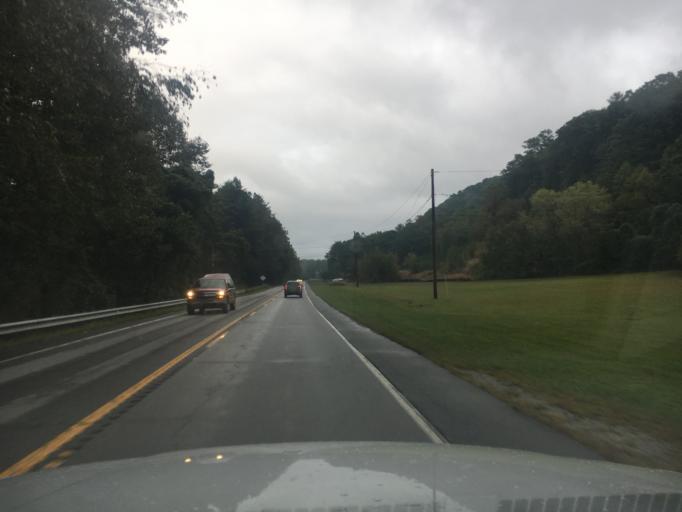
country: US
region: North Carolina
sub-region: Henderson County
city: Horse Shoe
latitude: 35.3316
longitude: -82.5723
